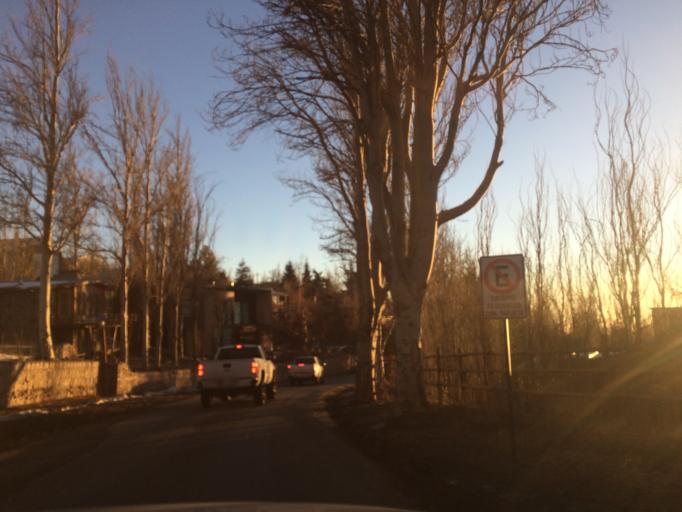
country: CL
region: Santiago Metropolitan
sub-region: Provincia de Santiago
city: Villa Presidente Frei, Nunoa, Santiago, Chile
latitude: -33.3506
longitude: -70.3097
